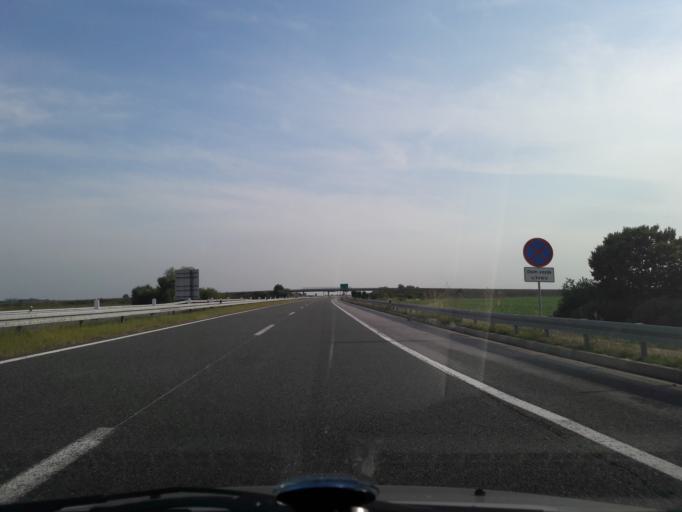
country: HR
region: Osjecko-Baranjska
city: Josipovac
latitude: 45.5707
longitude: 18.5502
